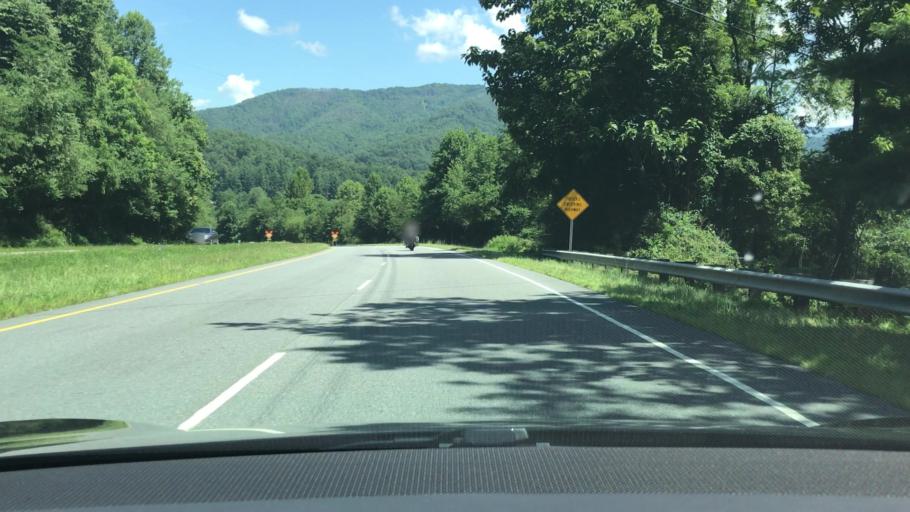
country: US
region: North Carolina
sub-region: Jackson County
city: Sylva
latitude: 35.3619
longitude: -83.2506
